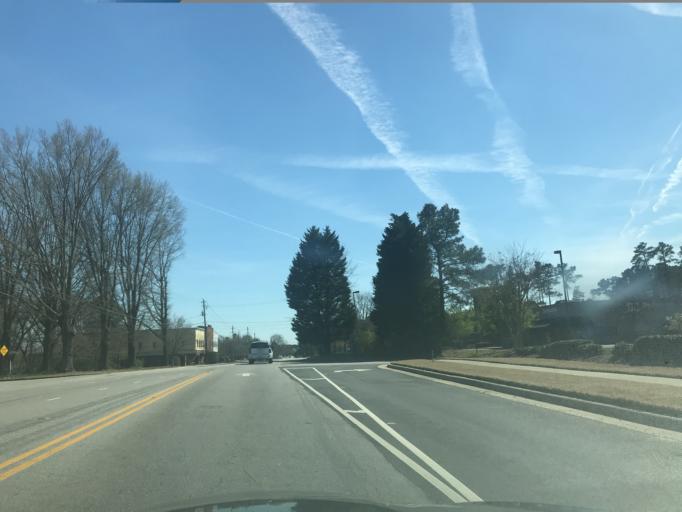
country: US
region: North Carolina
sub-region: Wake County
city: Fuquay-Varina
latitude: 35.5913
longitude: -78.7737
